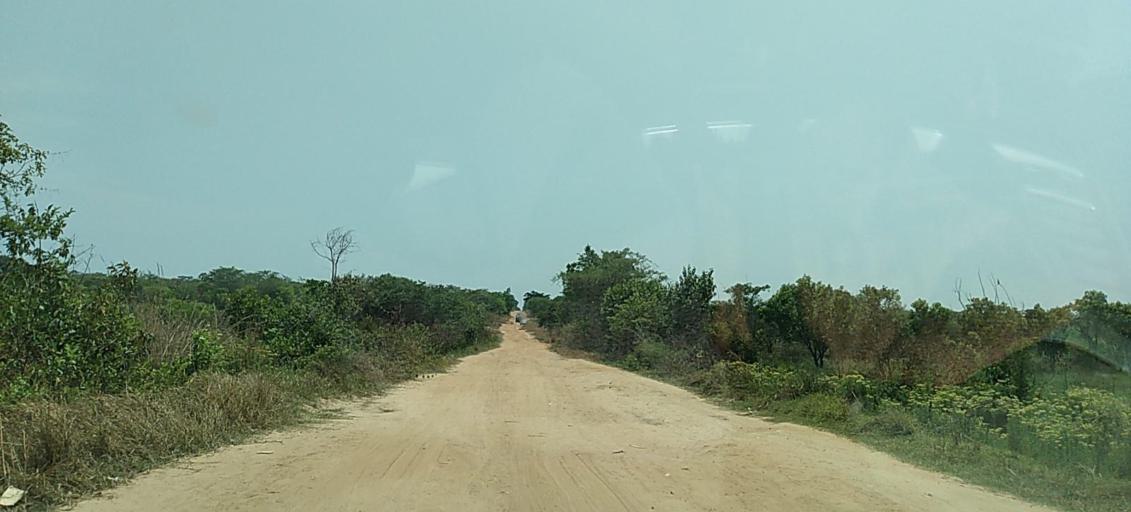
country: ZM
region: Copperbelt
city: Kalulushi
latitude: -12.9327
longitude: 28.1640
